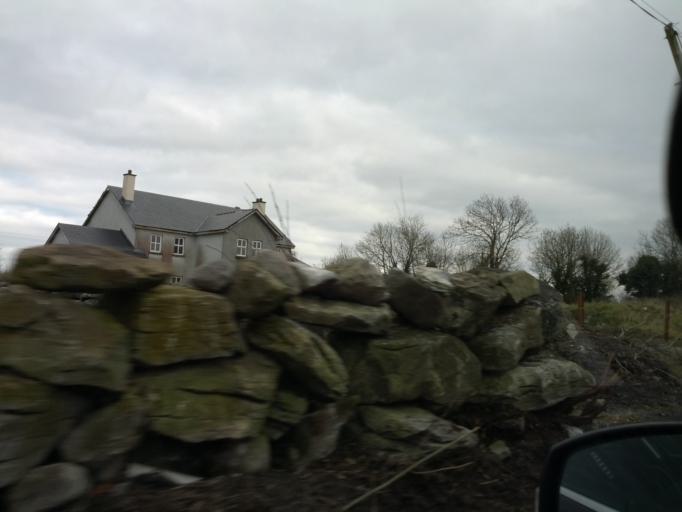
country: IE
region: Connaught
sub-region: County Galway
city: Oranmore
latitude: 53.1723
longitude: -8.8905
